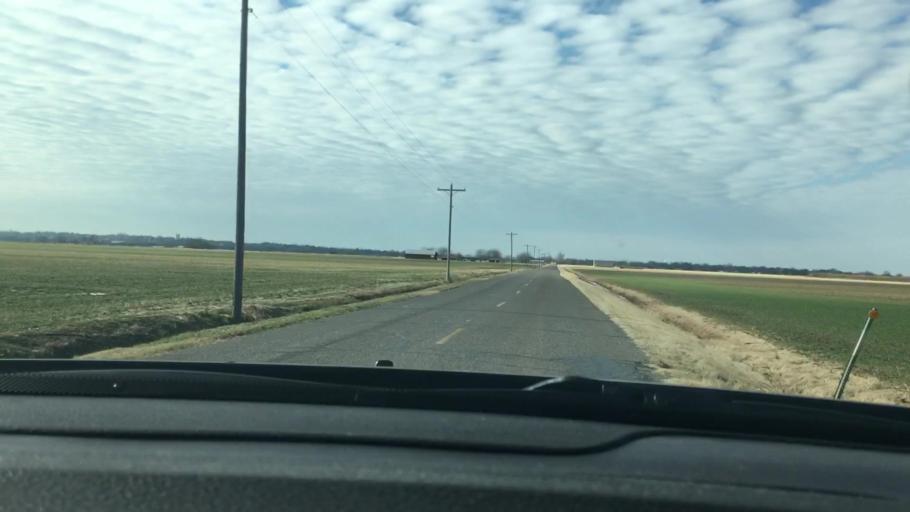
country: US
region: Oklahoma
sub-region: Garvin County
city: Pauls Valley
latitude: 34.7387
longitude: -97.1780
